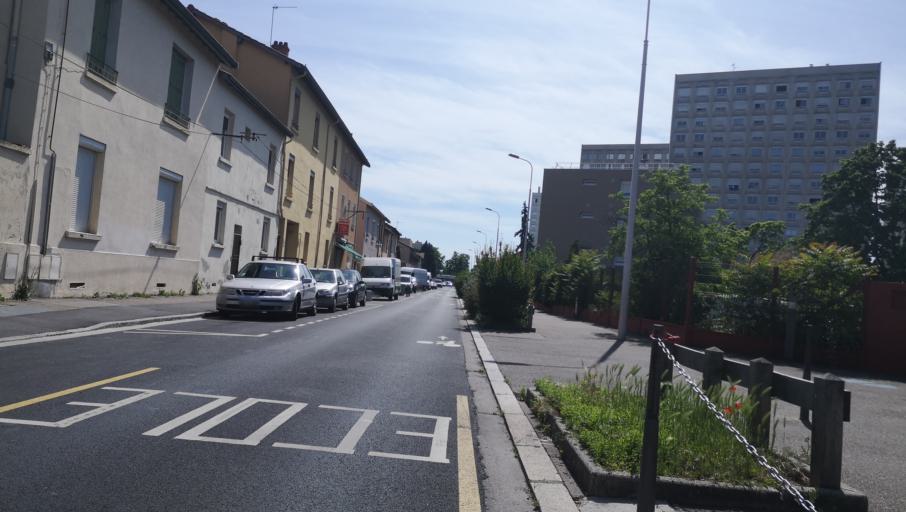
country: FR
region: Rhone-Alpes
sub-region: Departement du Rhone
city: Saint-Fons
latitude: 45.7268
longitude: 4.8750
